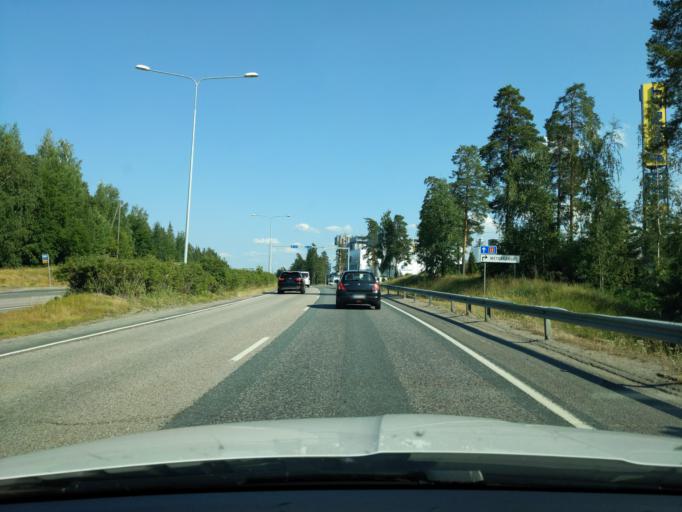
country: FI
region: Paijanne Tavastia
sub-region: Lahti
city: Lahti
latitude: 60.9818
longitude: 25.5914
